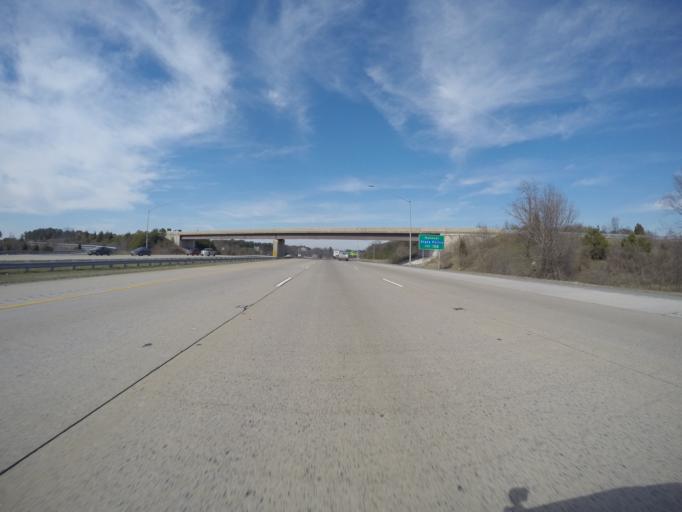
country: US
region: Maryland
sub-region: Anne Arundel County
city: Glen Burnie
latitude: 39.1517
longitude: -76.6451
